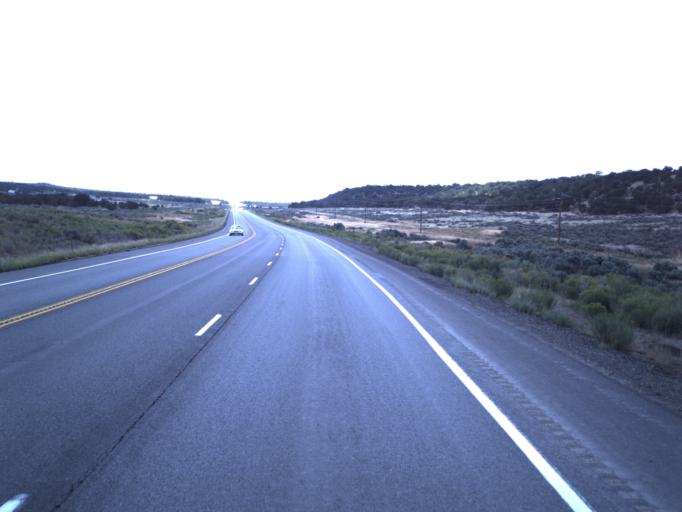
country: US
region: Utah
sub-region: Duchesne County
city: Duchesne
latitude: 40.1797
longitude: -110.6050
